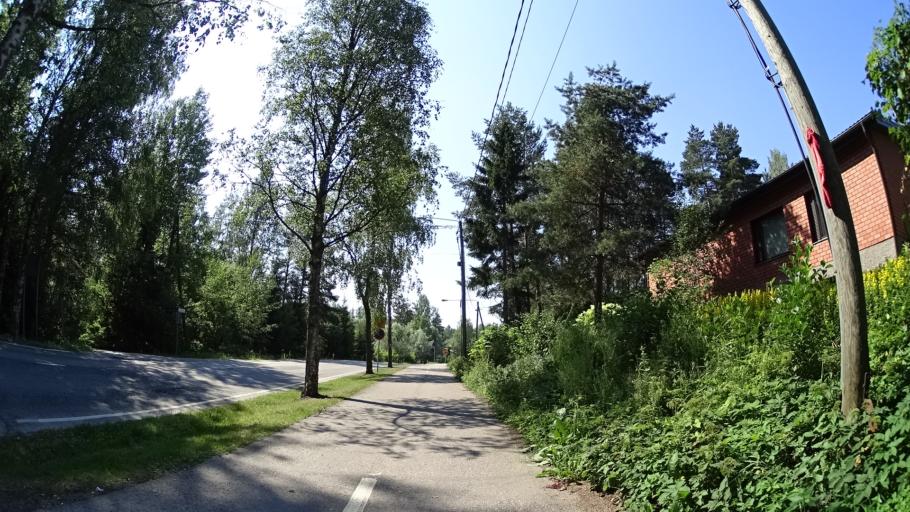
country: FI
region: Uusimaa
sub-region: Helsinki
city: Kerava
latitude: 60.3746
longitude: 25.0791
